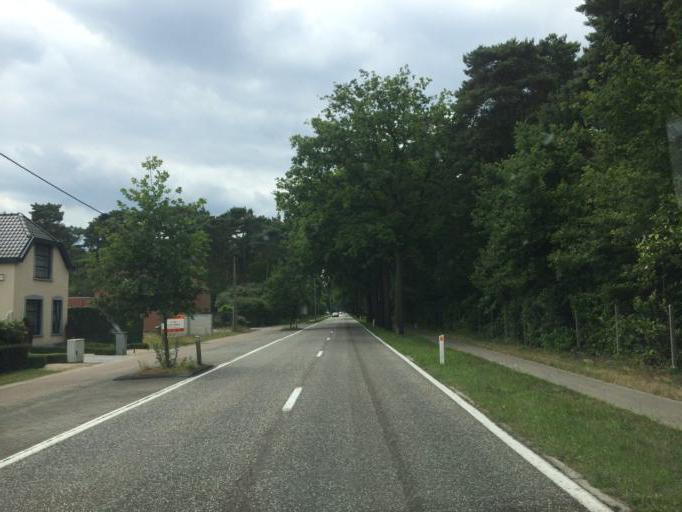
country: BE
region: Flanders
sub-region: Provincie Antwerpen
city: Balen
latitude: 51.2113
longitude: 5.1780
